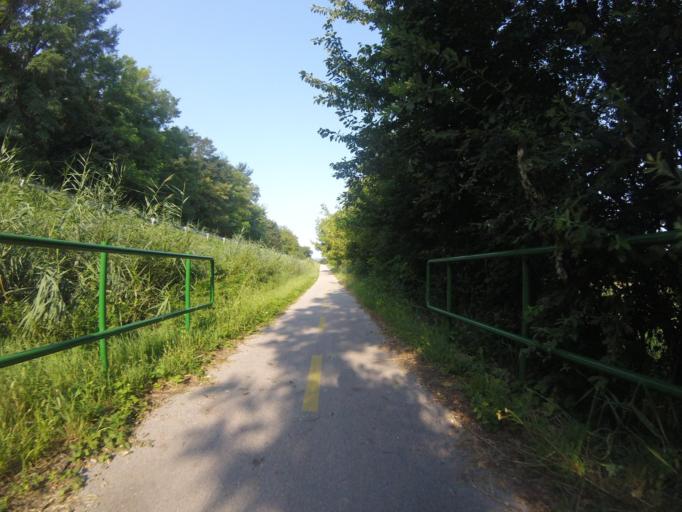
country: HU
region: Gyor-Moson-Sopron
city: Nagycenk
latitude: 47.6342
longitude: 16.7152
